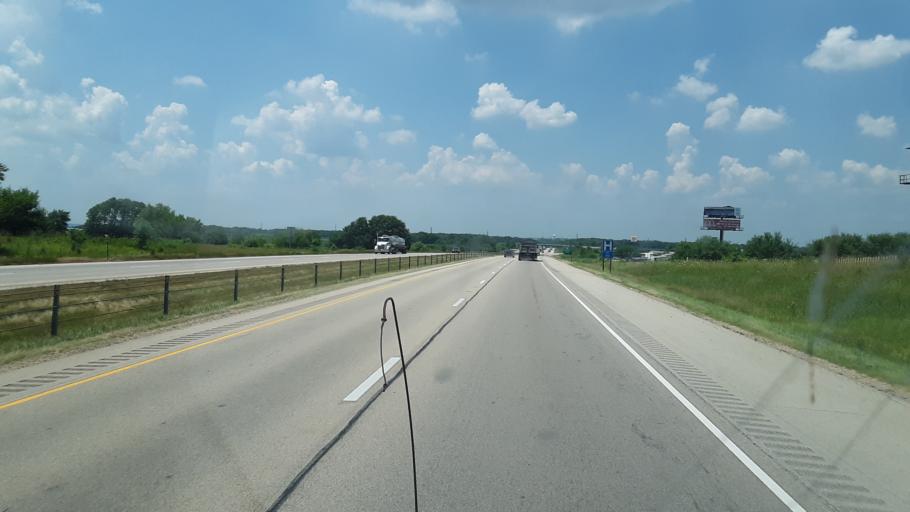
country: US
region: Illinois
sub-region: LaSalle County
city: Marseilles
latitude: 41.3757
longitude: -88.7658
